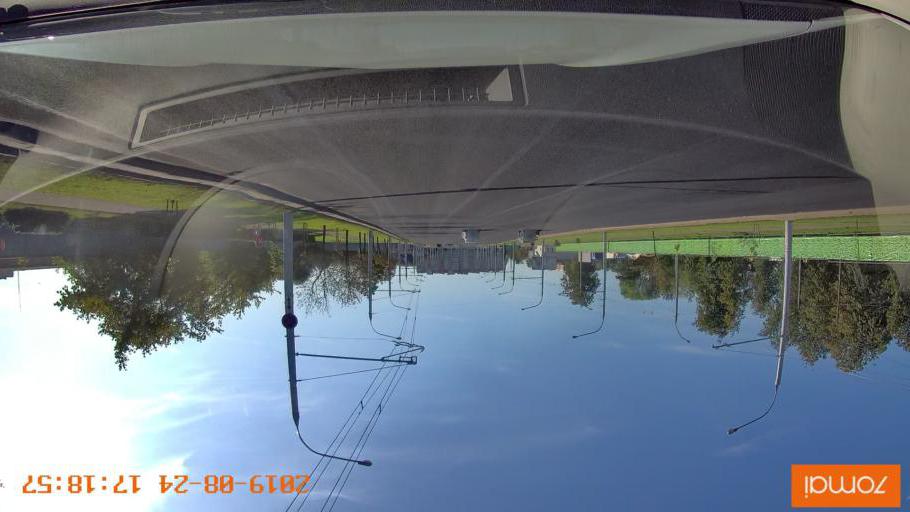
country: BY
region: Minsk
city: Vyaliki Trastsyanets
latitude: 53.8656
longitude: 27.6440
